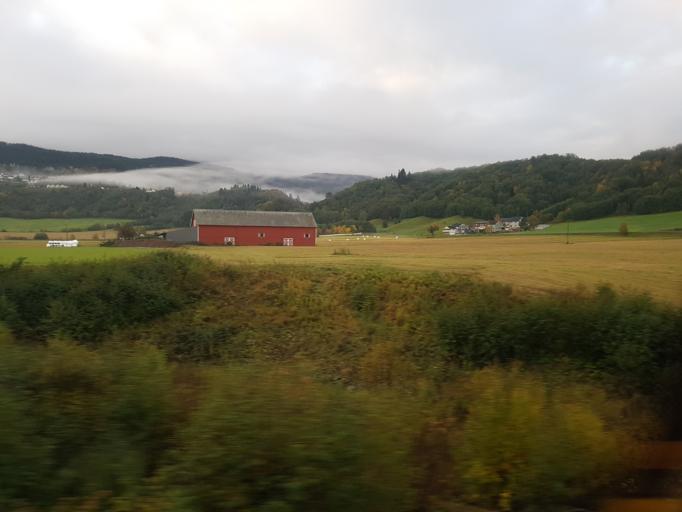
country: NO
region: Sor-Trondelag
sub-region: Melhus
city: Melhus
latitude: 63.2986
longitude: 10.2878
